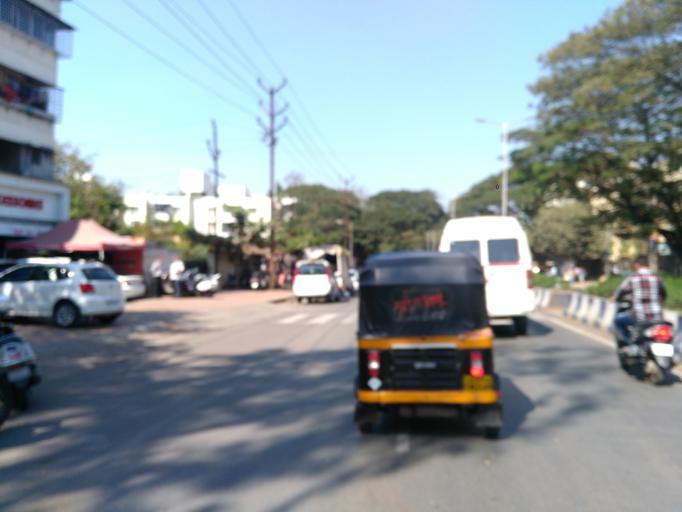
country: IN
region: Maharashtra
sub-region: Pune Division
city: Pune
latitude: 18.4697
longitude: 73.8639
